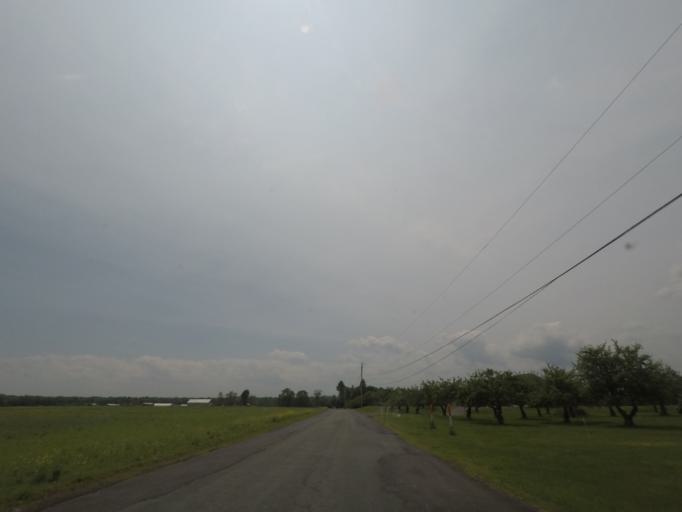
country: US
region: New York
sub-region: Rensselaer County
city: East Greenbush
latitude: 42.5404
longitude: -73.7025
